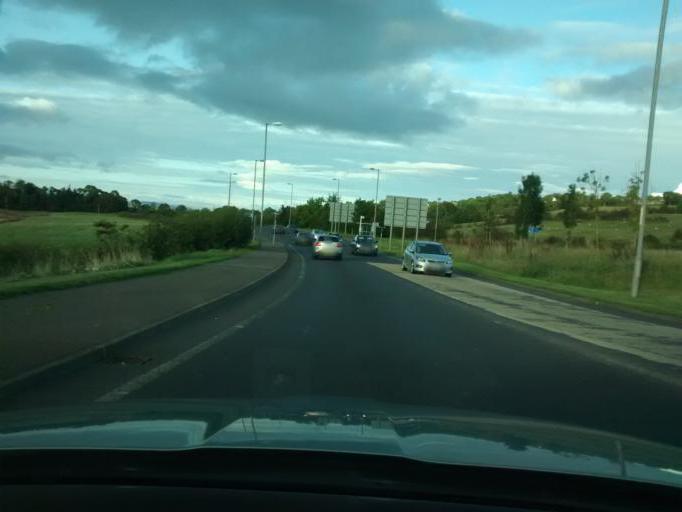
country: GB
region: Scotland
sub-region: Renfrewshire
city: Lochwinnoch
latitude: 55.7855
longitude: -4.6078
